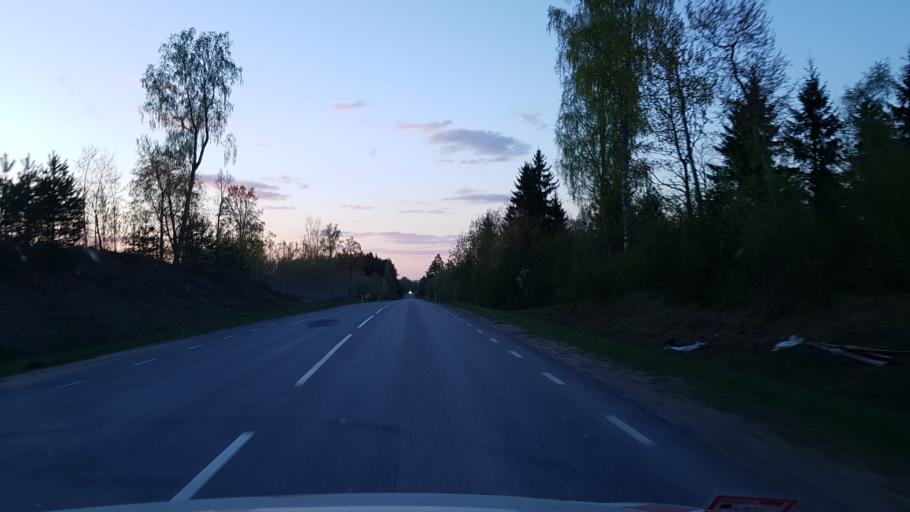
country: EE
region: Vorumaa
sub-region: Voru linn
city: Voru
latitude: 57.7876
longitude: 27.0347
